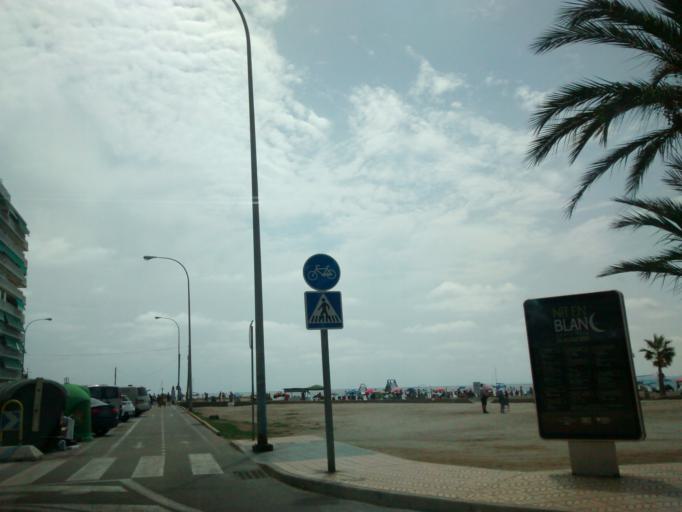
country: ES
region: Valencia
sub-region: Provincia de Alicante
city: Santa Pola
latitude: 38.1923
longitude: -0.5657
